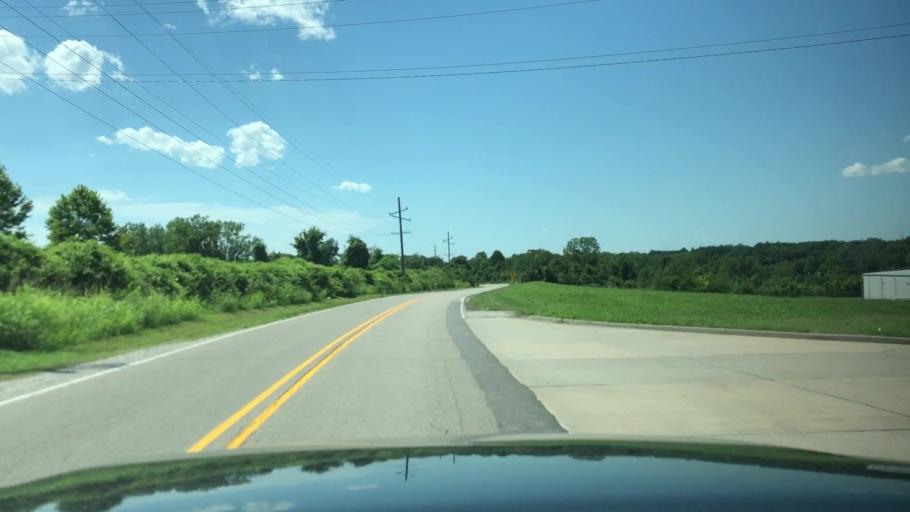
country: US
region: Illinois
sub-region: Saint Clair County
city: Alorton
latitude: 38.5532
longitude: -90.0796
